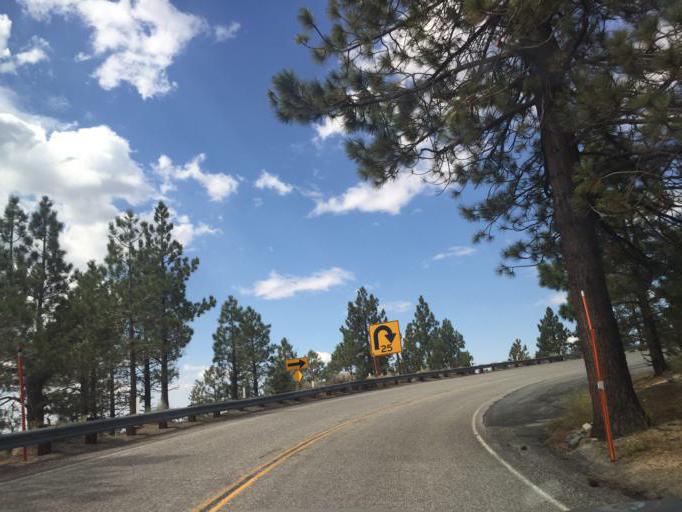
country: US
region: California
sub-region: Los Angeles County
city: Littlerock
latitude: 34.3546
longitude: -117.9472
